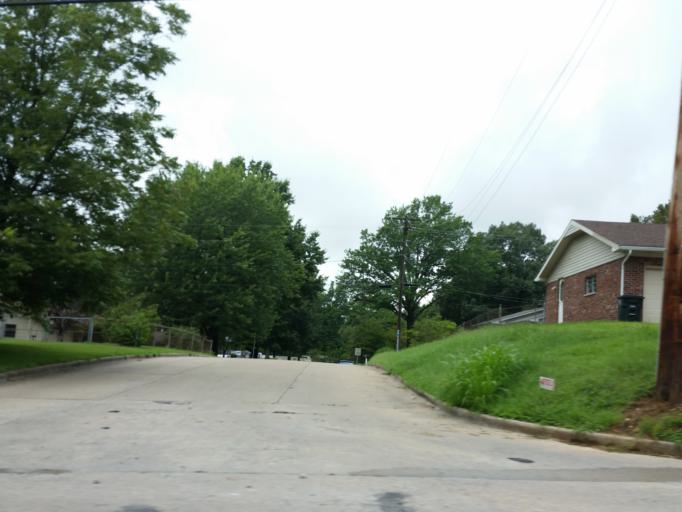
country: US
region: Missouri
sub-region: Cape Girardeau County
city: Cape Girardeau
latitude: 37.3357
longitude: -89.5507
